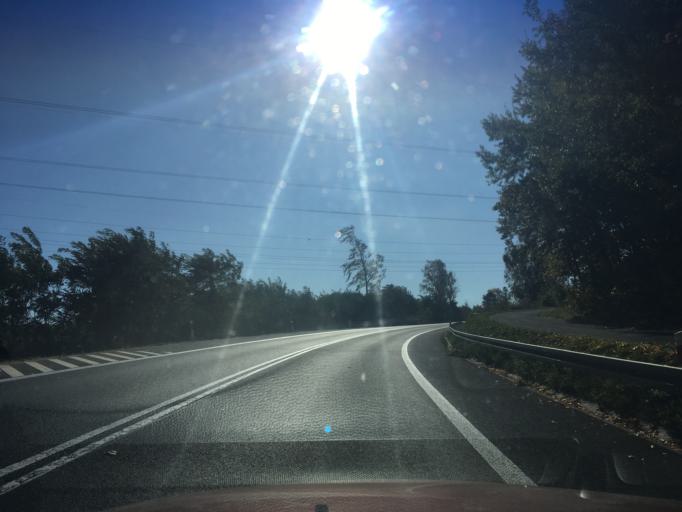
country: DE
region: Saxony
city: Ostritz
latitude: 50.9904
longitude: 14.9439
